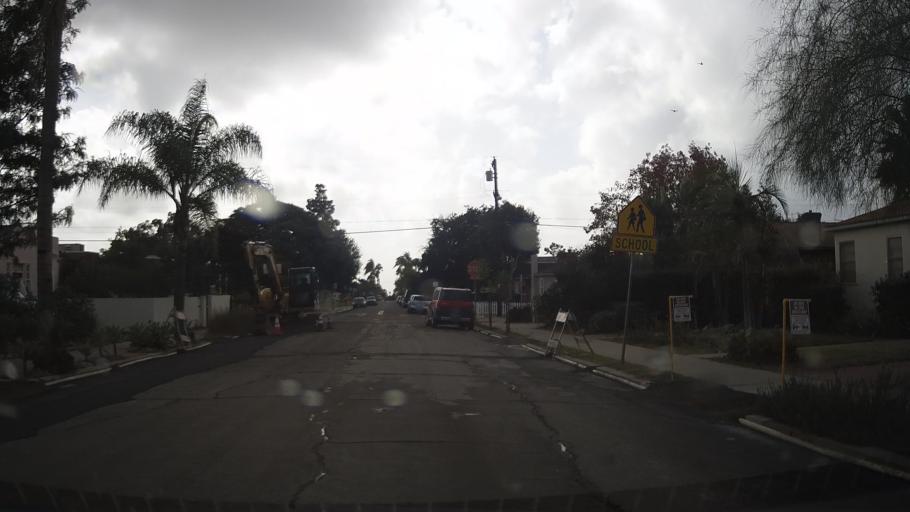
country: US
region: California
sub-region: San Diego County
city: San Diego
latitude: 32.7379
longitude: -117.1222
